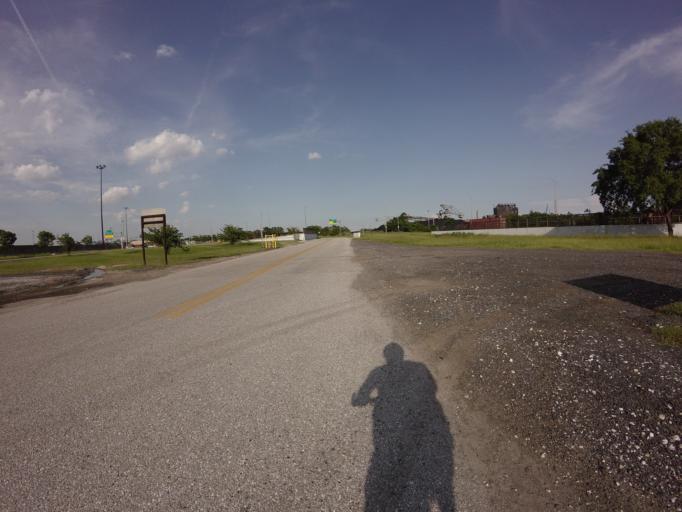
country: US
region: Maryland
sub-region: Baltimore County
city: Dundalk
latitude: 39.2641
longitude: -76.5643
